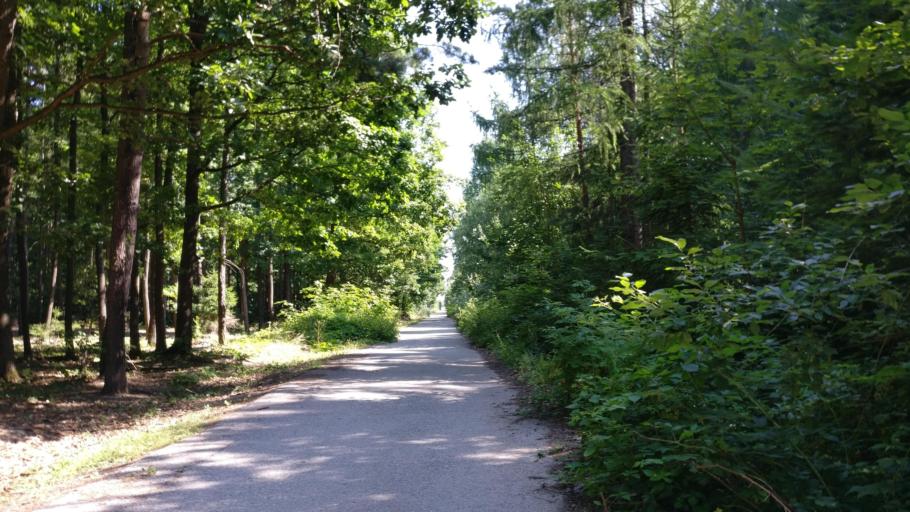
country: CZ
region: South Moravian
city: Zbraslav
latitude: 49.2142
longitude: 16.2807
